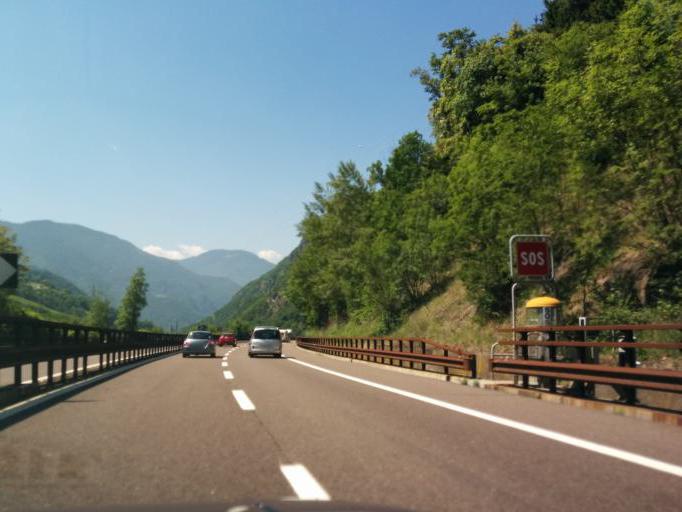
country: IT
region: Trentino-Alto Adige
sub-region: Bolzano
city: Fie Allo Sciliar
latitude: 46.5137
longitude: 11.4754
